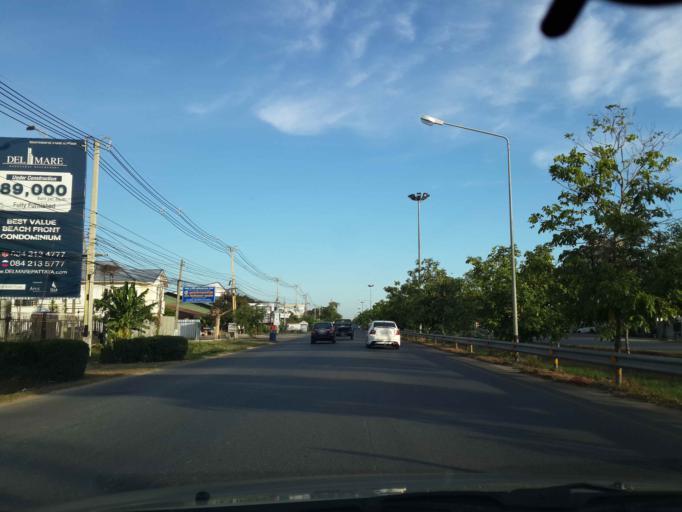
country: TH
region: Chon Buri
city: Phatthaya
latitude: 12.8480
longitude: 100.9095
